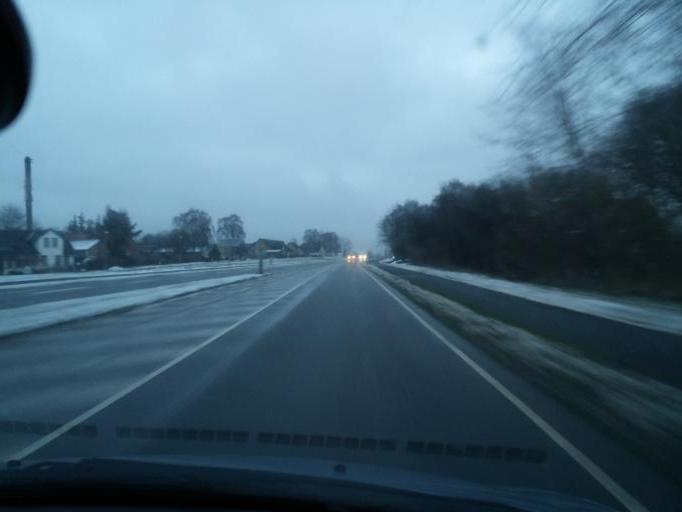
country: DK
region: South Denmark
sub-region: Kerteminde Kommune
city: Munkebo
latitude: 55.4565
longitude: 10.5595
